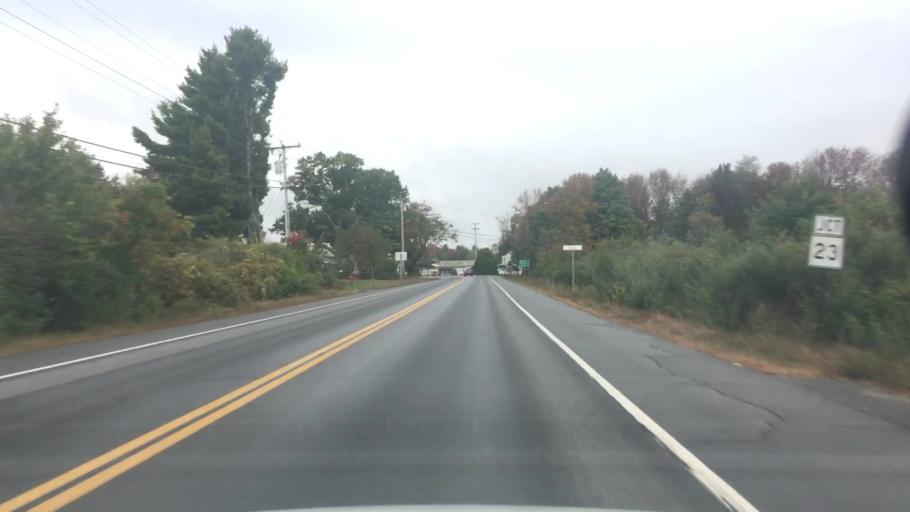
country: US
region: Maine
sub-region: Kennebec County
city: Belgrade
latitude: 44.3933
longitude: -69.8027
